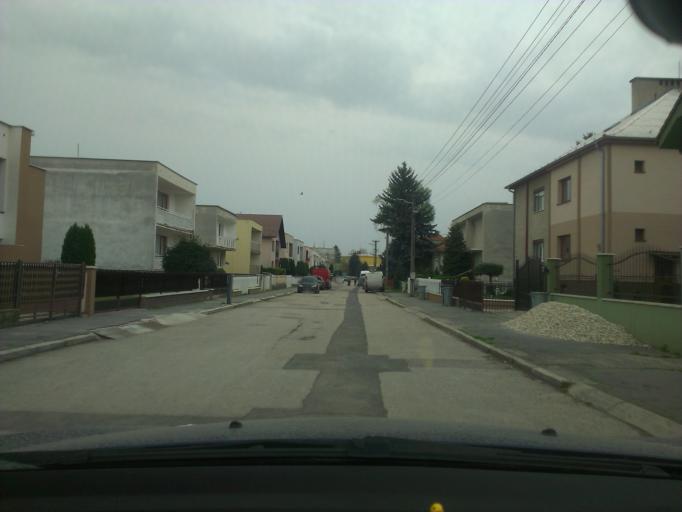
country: SK
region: Trnavsky
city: Vrbove
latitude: 48.6250
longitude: 17.7193
